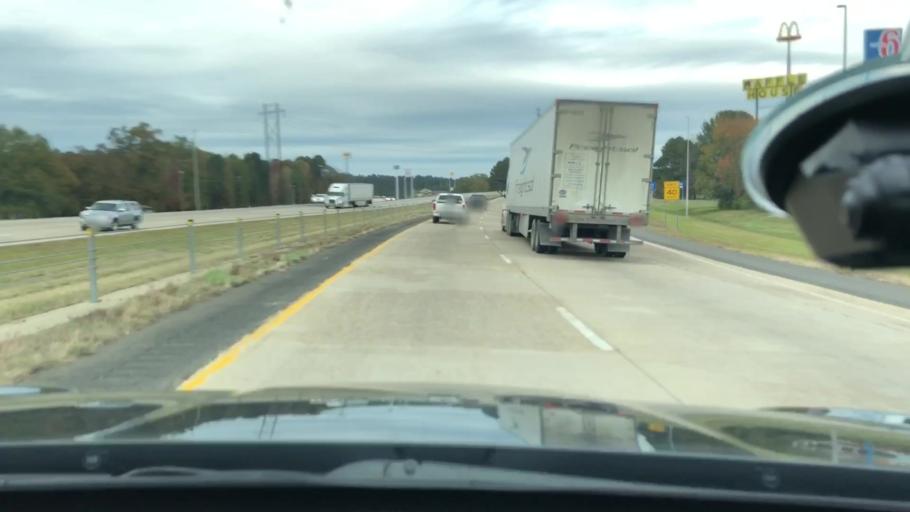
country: US
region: Arkansas
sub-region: Clark County
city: Arkadelphia
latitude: 34.1814
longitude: -93.0730
